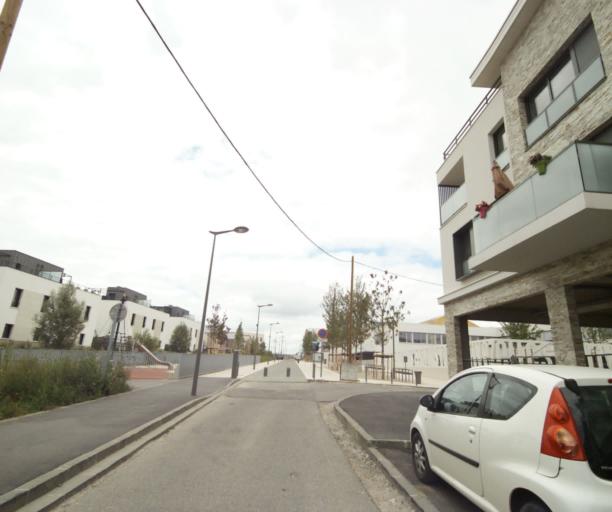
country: FR
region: Ile-de-France
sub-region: Departement des Yvelines
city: Saint-Cyr-l'Ecole
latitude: 48.8068
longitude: 2.0680
